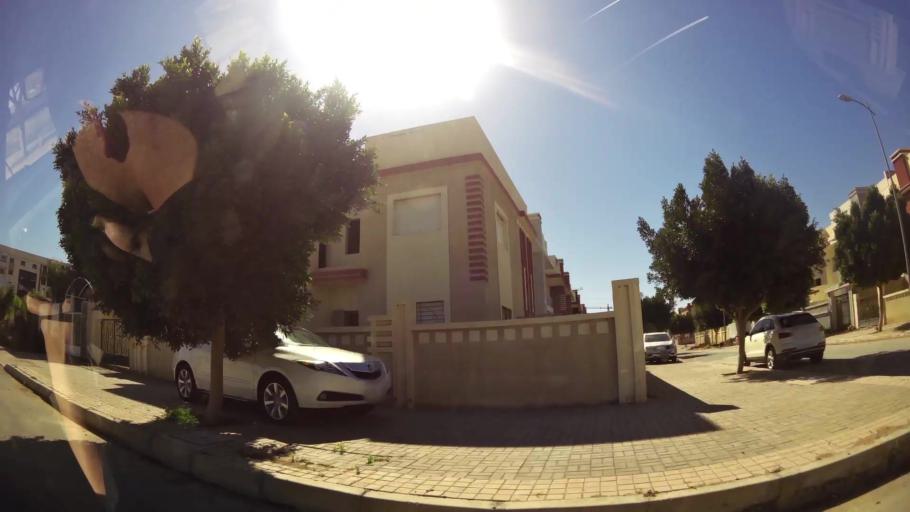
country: MA
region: Oriental
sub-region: Oujda-Angad
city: Oujda
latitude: 34.7233
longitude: -1.9079
